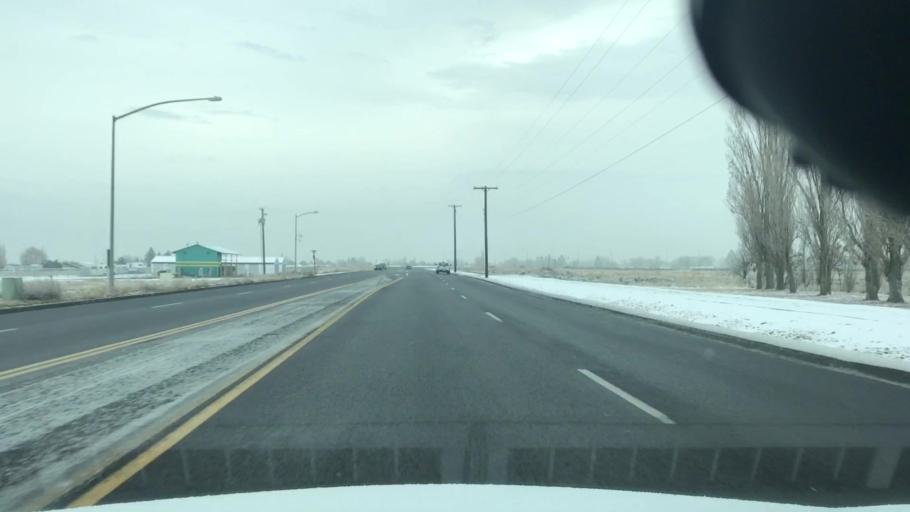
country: US
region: Washington
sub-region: Grant County
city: Cascade Valley
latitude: 47.1614
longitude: -119.3128
